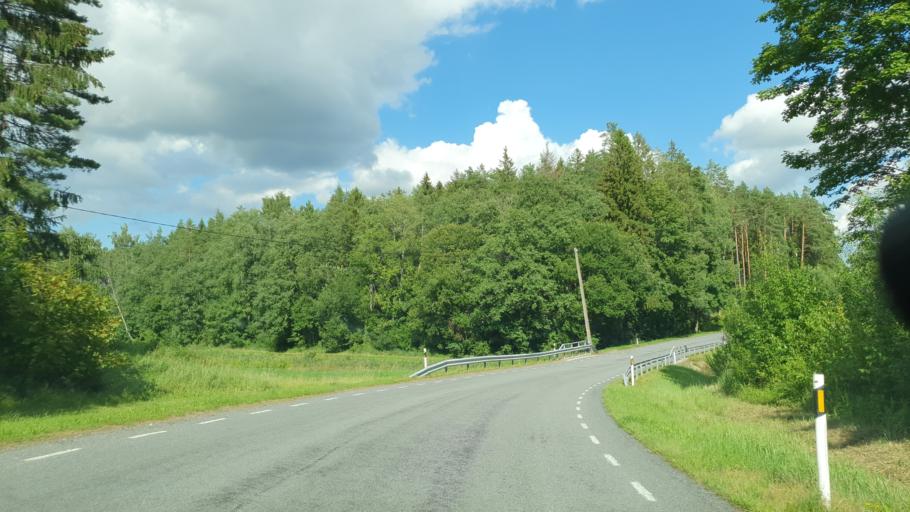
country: EE
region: Jogevamaa
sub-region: Tabivere vald
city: Tabivere
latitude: 58.6295
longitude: 26.5901
